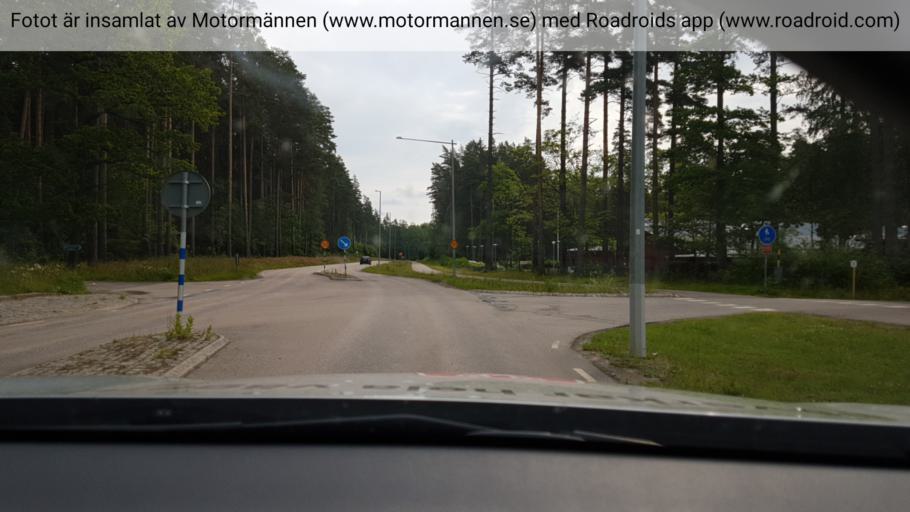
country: SE
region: Vaestra Goetaland
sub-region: Skovde Kommun
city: Skultorp
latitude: 58.3412
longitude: 13.8481
